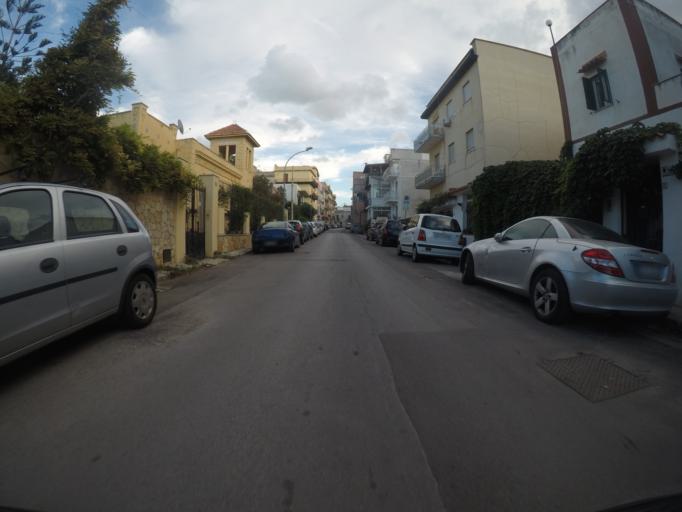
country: IT
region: Sicily
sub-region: Palermo
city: Isola delle Femmine
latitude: 38.2011
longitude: 13.2775
